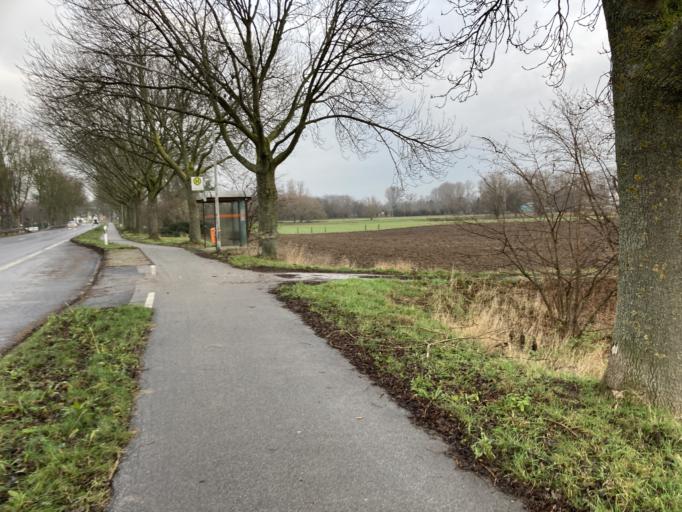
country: DE
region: North Rhine-Westphalia
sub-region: Regierungsbezirk Dusseldorf
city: Neubrueck
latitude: 51.1209
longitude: 6.6260
